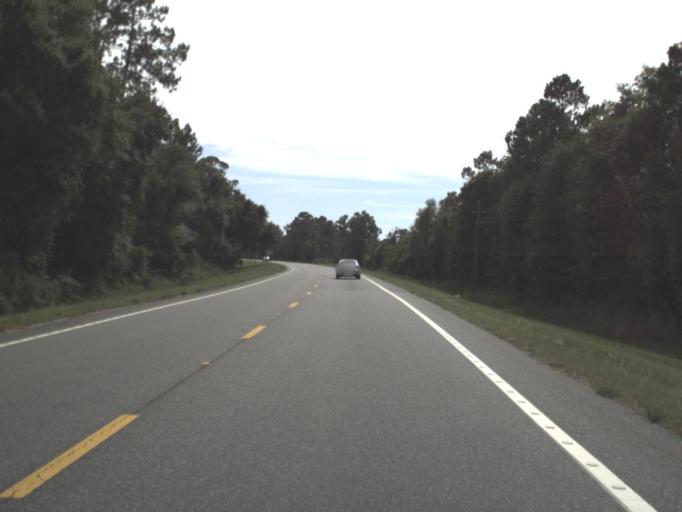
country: US
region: Florida
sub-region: Taylor County
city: Perry
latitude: 30.0936
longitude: -83.4898
